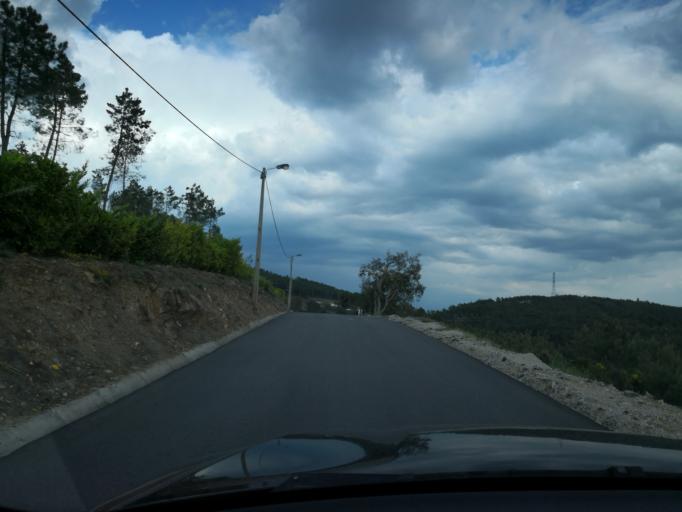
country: PT
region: Vila Real
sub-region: Sabrosa
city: Vilela
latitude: 41.2222
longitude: -7.6815
